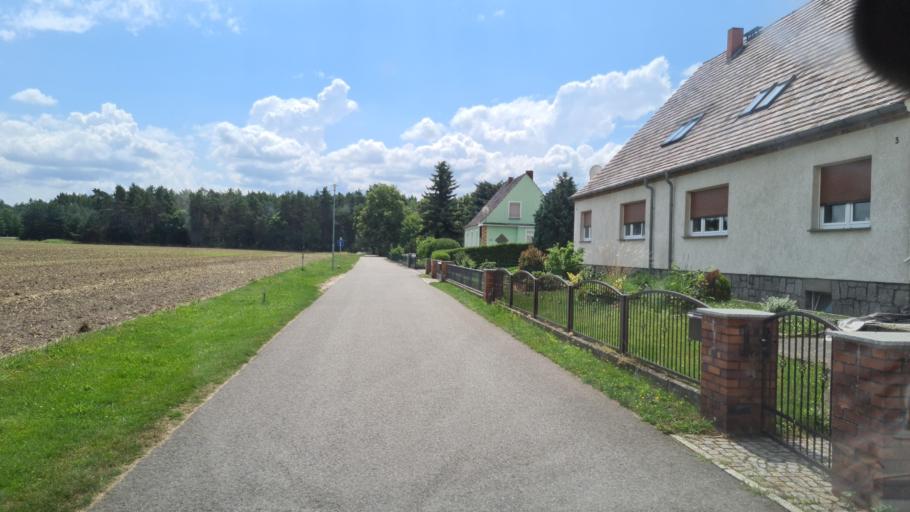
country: DE
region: Brandenburg
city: Welzow
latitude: 51.5187
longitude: 14.1766
